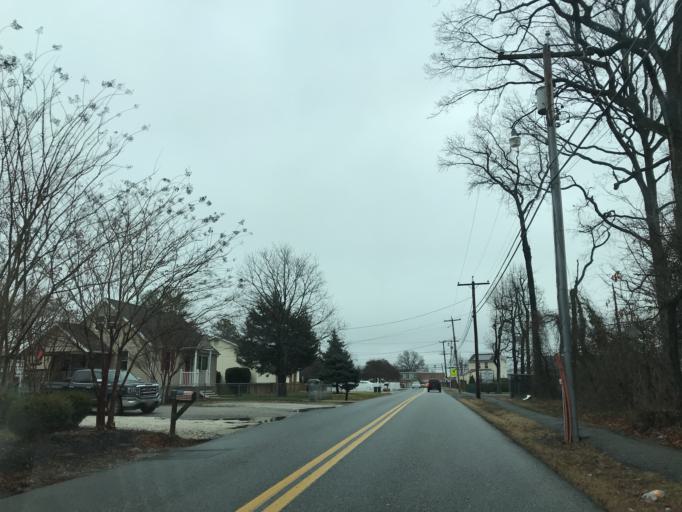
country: US
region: Maryland
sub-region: Baltimore County
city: Edgemere
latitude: 39.2360
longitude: -76.4446
